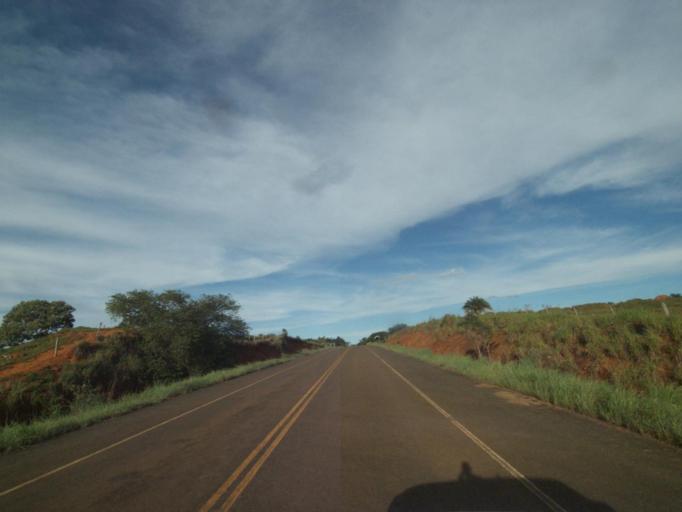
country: BR
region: Goias
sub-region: Jaragua
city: Jaragua
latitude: -15.8690
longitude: -49.4091
